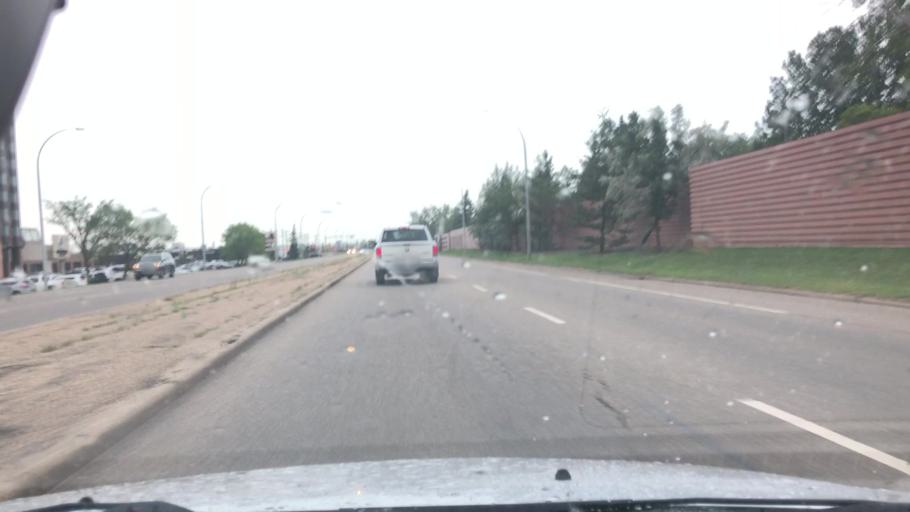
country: CA
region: Alberta
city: St. Albert
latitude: 53.5535
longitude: -113.6071
